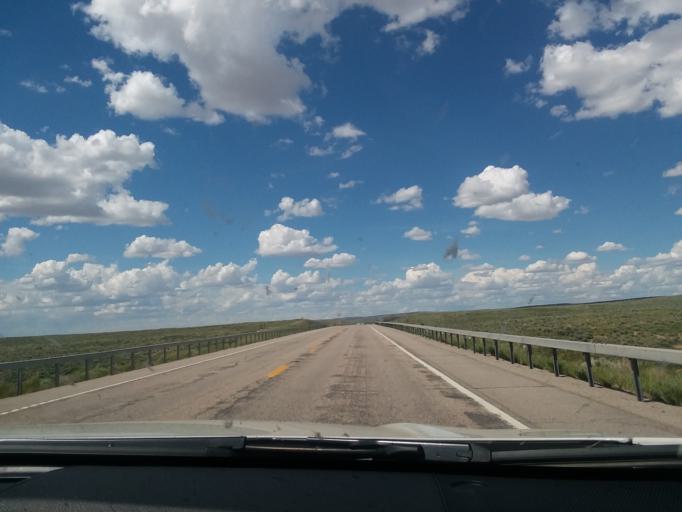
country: US
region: Wyoming
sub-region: Sweetwater County
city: North Rock Springs
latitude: 41.7690
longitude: -109.3407
